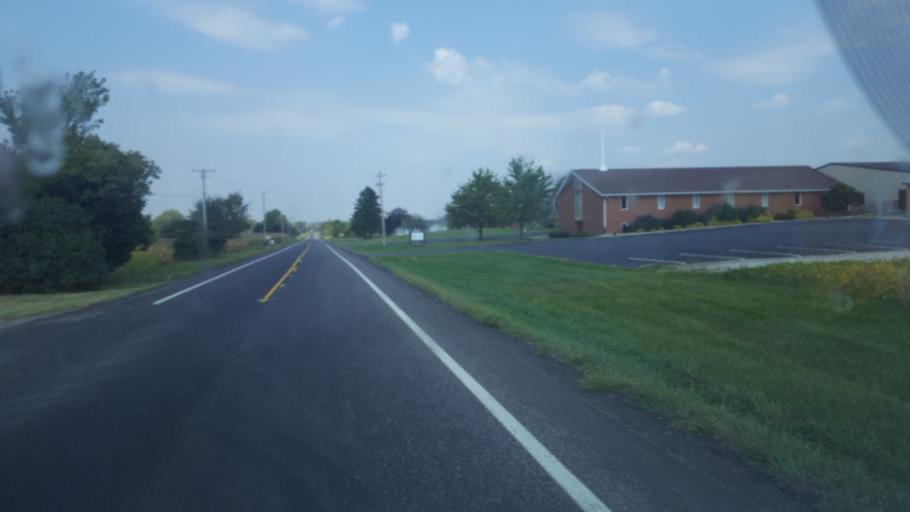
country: US
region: Ohio
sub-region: Richland County
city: Lexington
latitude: 40.5852
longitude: -82.6620
